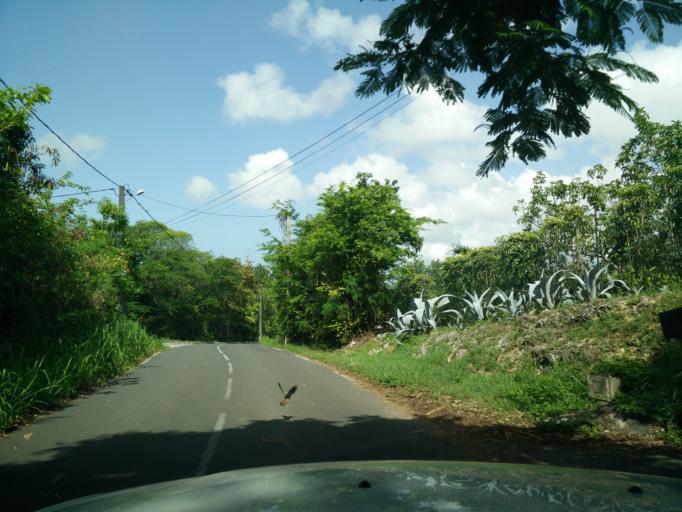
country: GP
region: Guadeloupe
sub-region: Guadeloupe
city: Le Gosier
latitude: 16.2298
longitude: -61.4699
